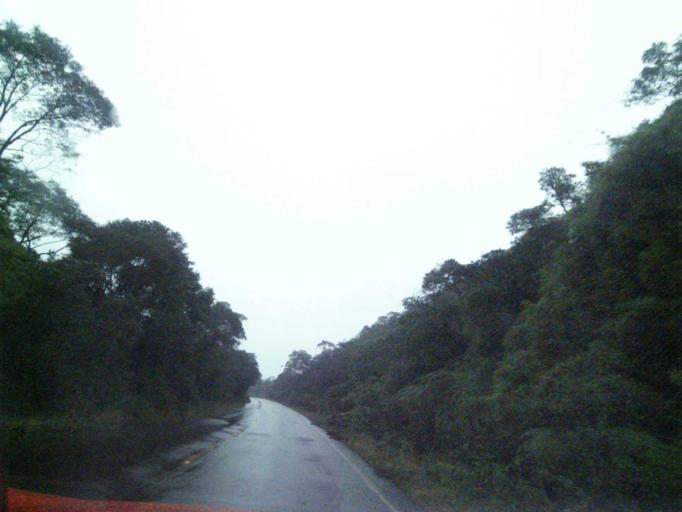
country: BR
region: Santa Catarina
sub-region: Anitapolis
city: Anitapolis
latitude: -27.7760
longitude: -49.0416
